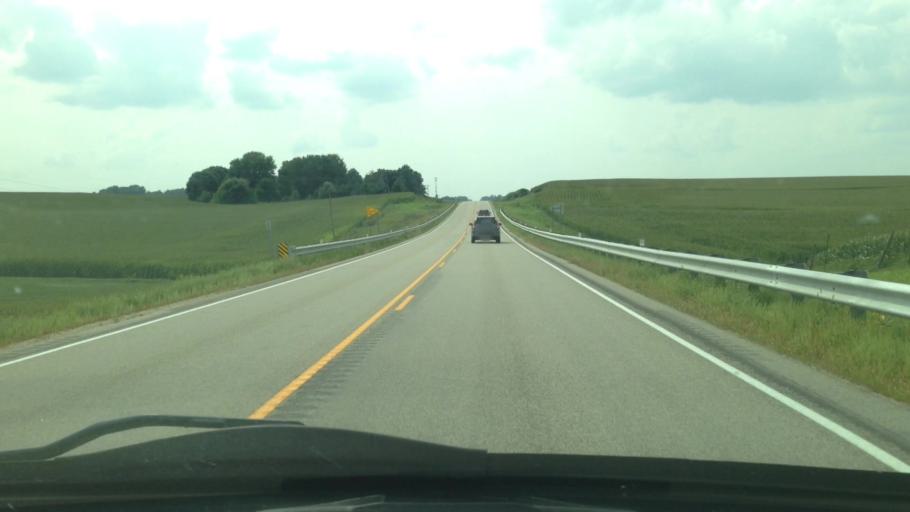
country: US
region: Minnesota
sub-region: Olmsted County
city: Oronoco
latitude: 44.1658
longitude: -92.4036
